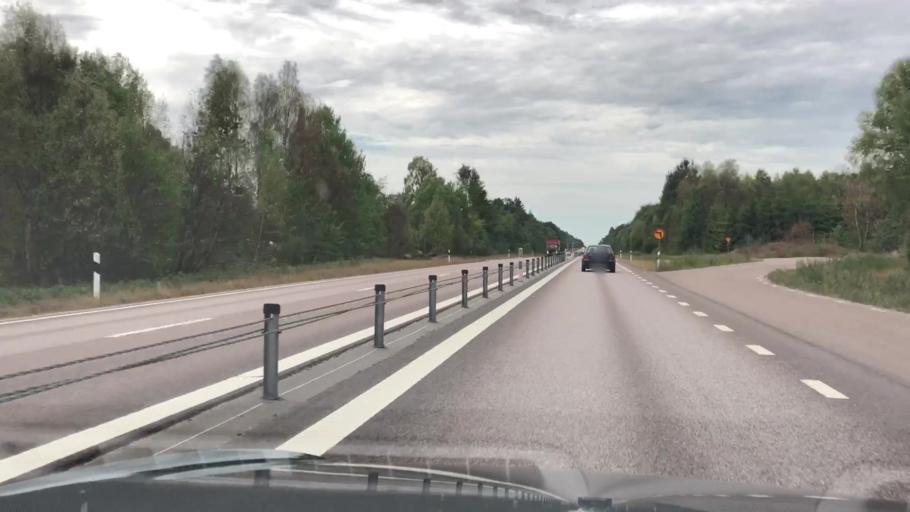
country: SE
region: Blekinge
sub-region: Karlskrona Kommun
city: Jaemjoe
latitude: 56.2103
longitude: 15.8763
